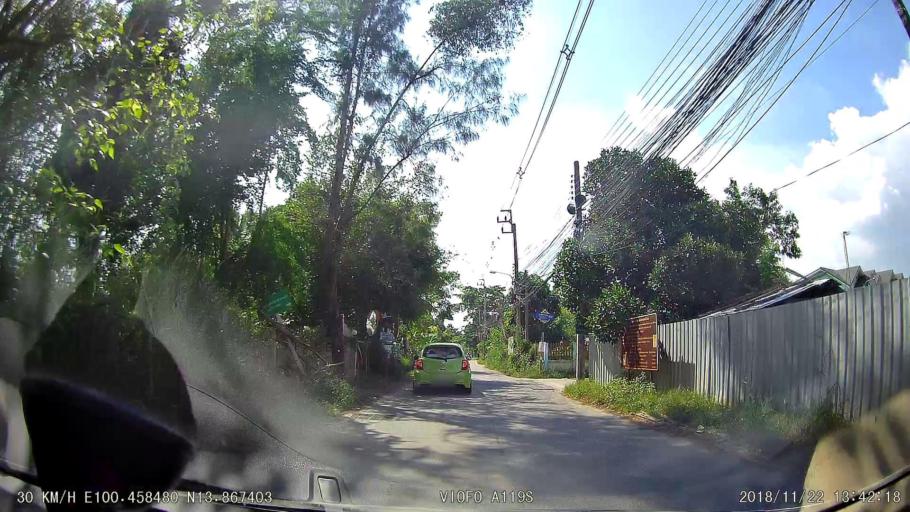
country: TH
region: Nonthaburi
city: Bang Bua Thong
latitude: 13.8674
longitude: 100.4584
